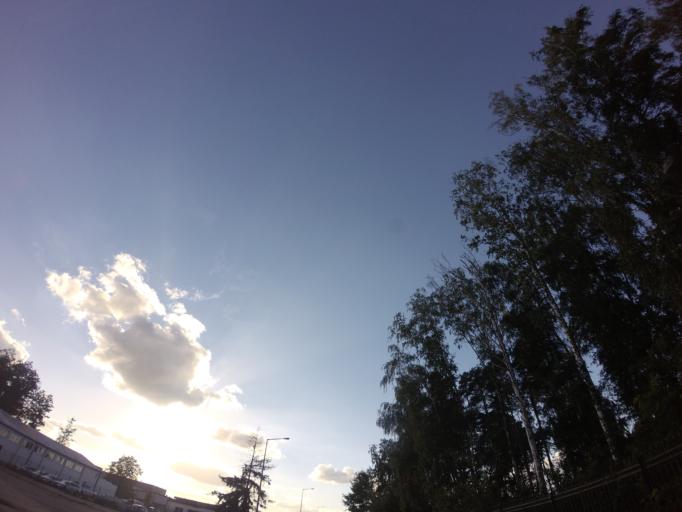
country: PL
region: Greater Poland Voivodeship
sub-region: Powiat nowotomyski
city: Nowy Tomysl
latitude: 52.3068
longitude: 16.1254
